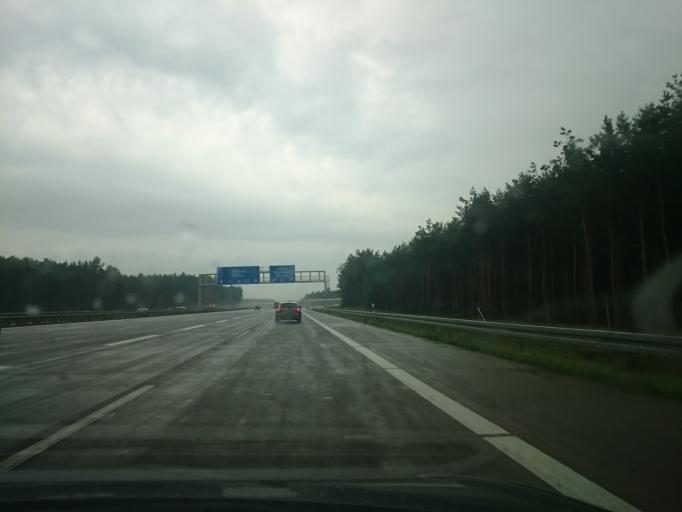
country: DE
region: Brandenburg
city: Kremmen
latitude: 52.7097
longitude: 13.0324
